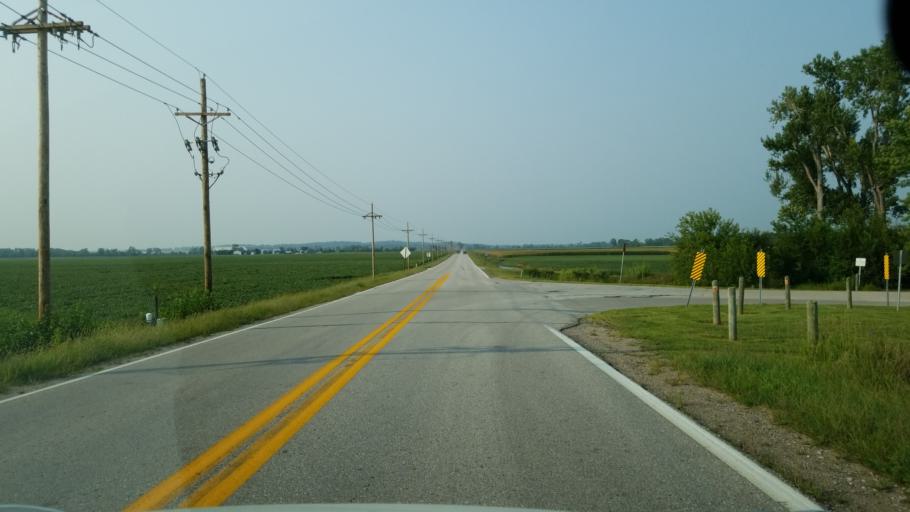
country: US
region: Nebraska
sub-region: Sarpy County
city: Offutt Air Force Base
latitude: 41.0830
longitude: -95.8898
